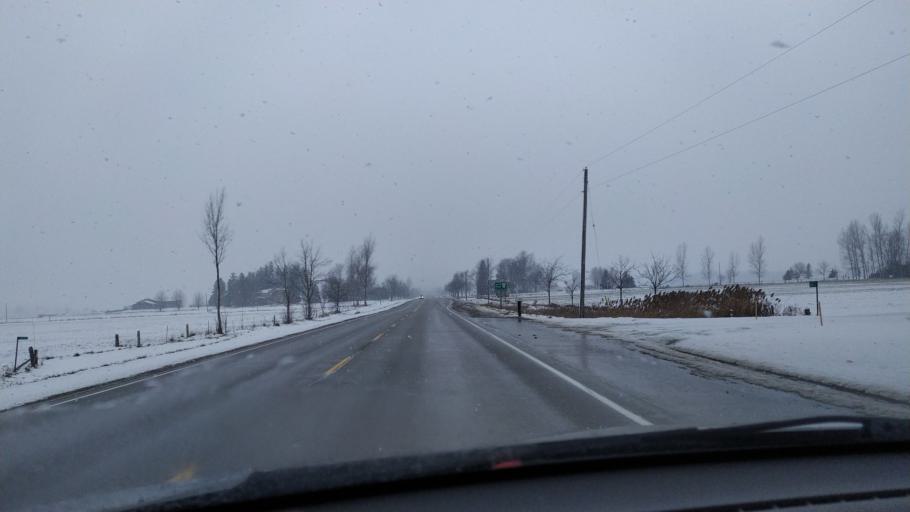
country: CA
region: Ontario
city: Stratford
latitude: 43.5055
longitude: -80.8868
